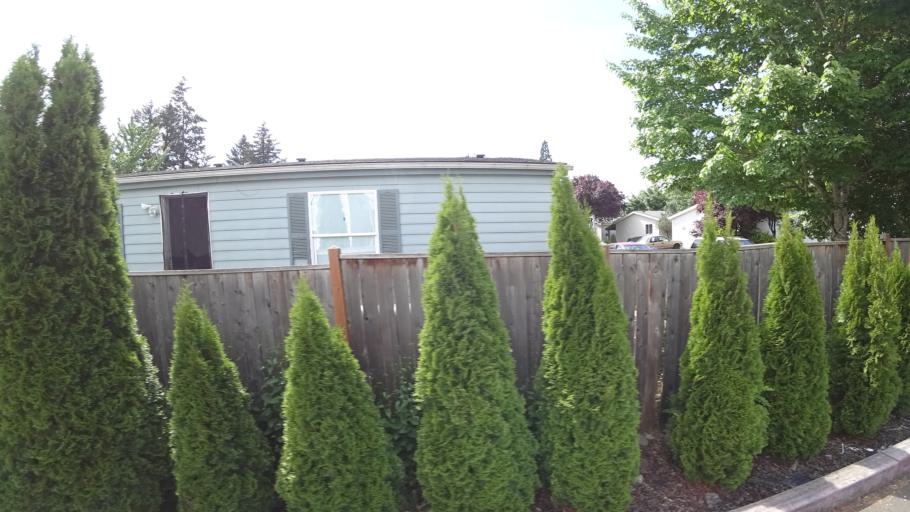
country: US
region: Oregon
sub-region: Multnomah County
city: Lents
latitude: 45.4905
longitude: -122.5401
